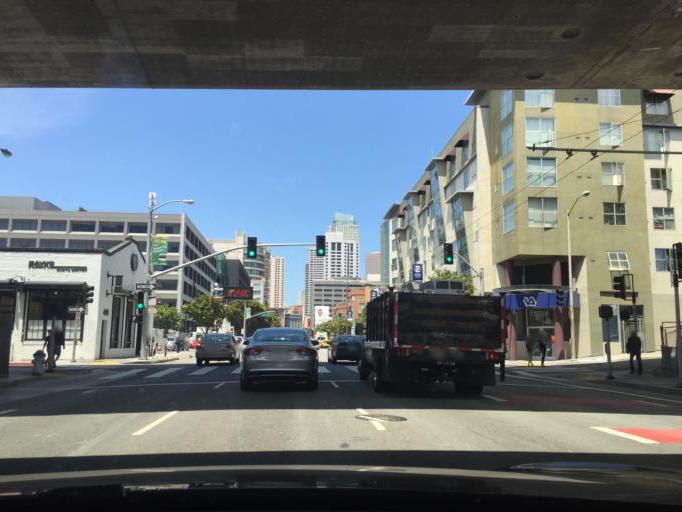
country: US
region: California
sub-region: San Francisco County
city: San Francisco
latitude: 37.7819
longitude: -122.3966
